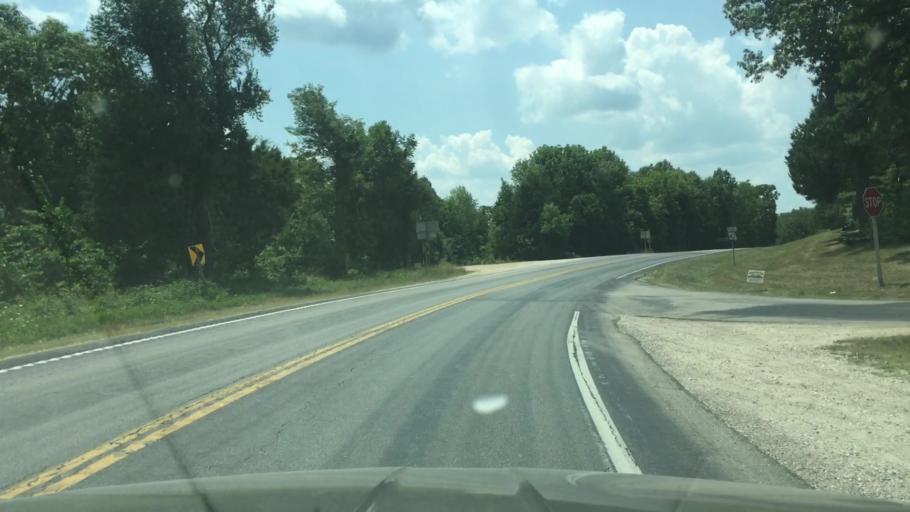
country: US
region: Missouri
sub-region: Camden County
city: Osage Beach
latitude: 38.1297
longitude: -92.5570
